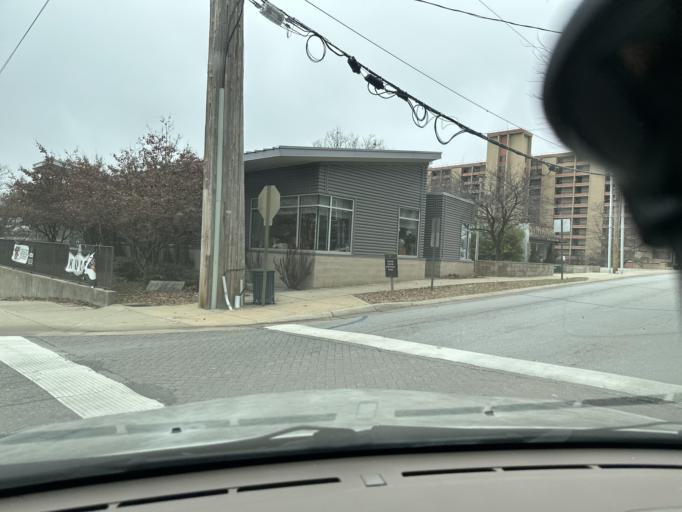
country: US
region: Arkansas
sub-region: Washington County
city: Fayetteville
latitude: 36.0620
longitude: -94.1643
